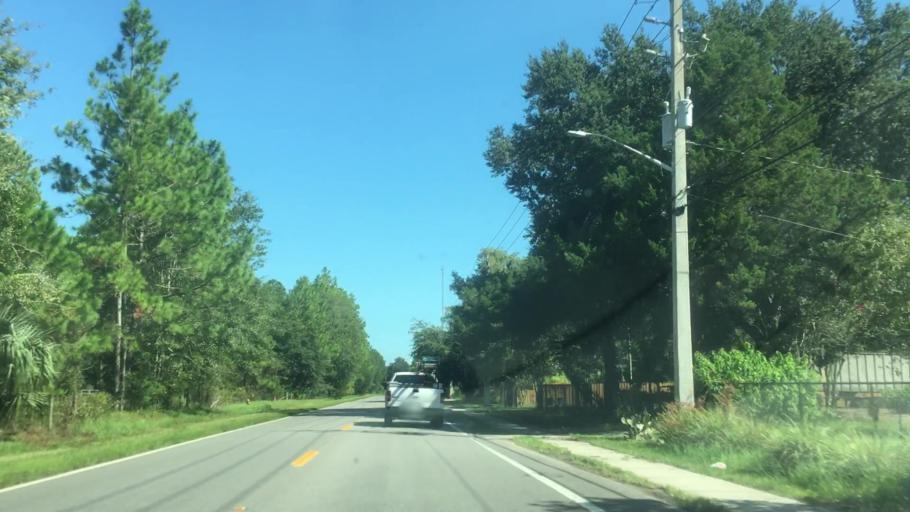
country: US
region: Florida
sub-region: Nassau County
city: Yulee
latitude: 30.4932
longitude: -81.5881
